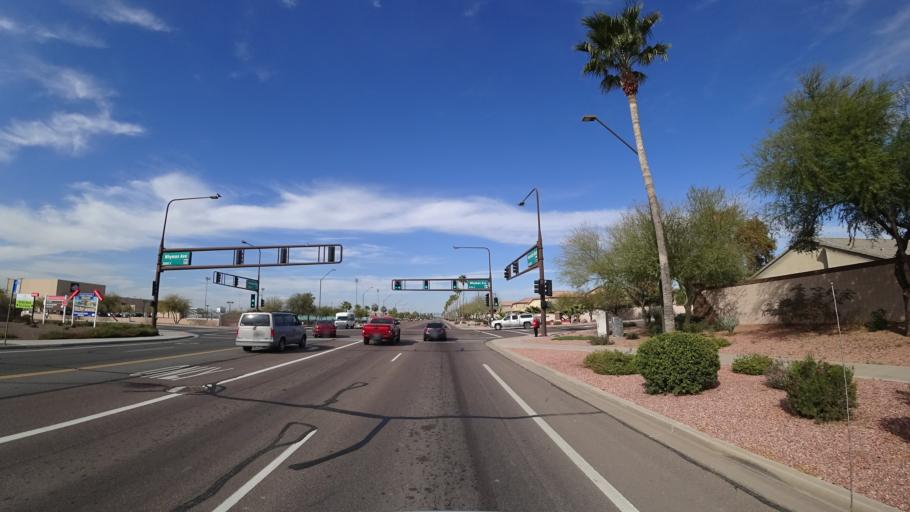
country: US
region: Arizona
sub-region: Maricopa County
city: Avondale
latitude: 33.4240
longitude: -112.3063
